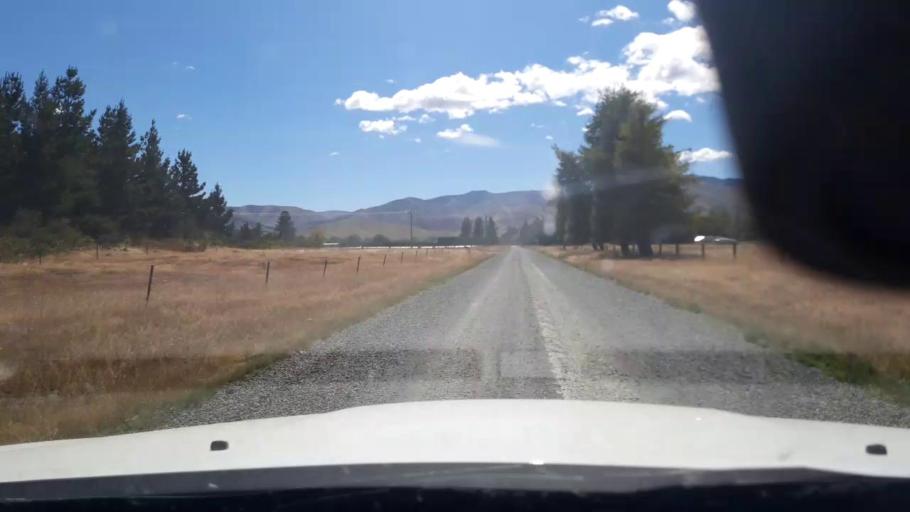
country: NZ
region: Canterbury
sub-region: Timaru District
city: Pleasant Point
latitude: -44.0021
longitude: 170.8349
